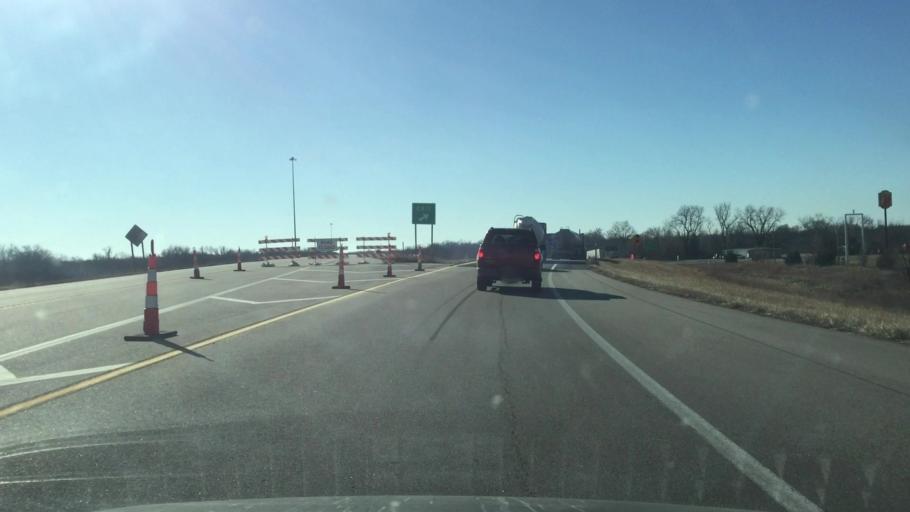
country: US
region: Kansas
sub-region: Allen County
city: Iola
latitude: 37.9248
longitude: -95.3798
